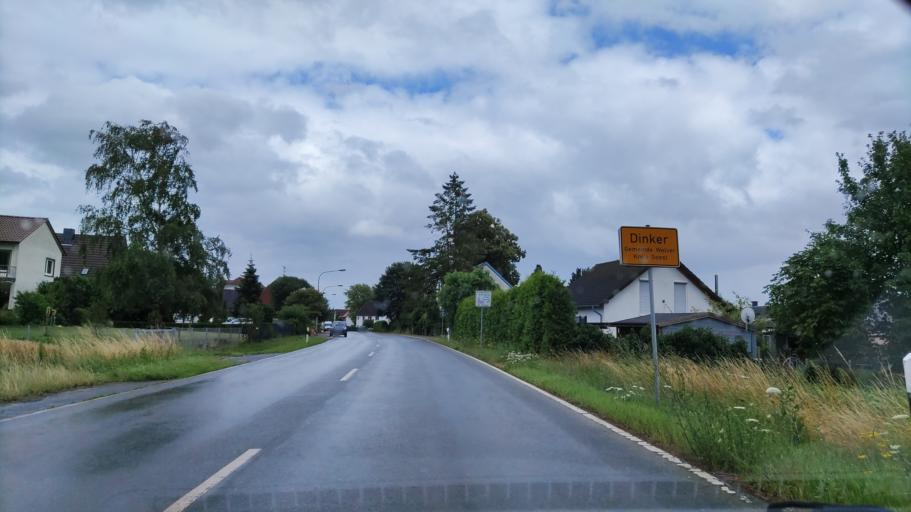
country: DE
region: North Rhine-Westphalia
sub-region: Regierungsbezirk Arnsberg
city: Welver
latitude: 51.6431
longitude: 7.9556
